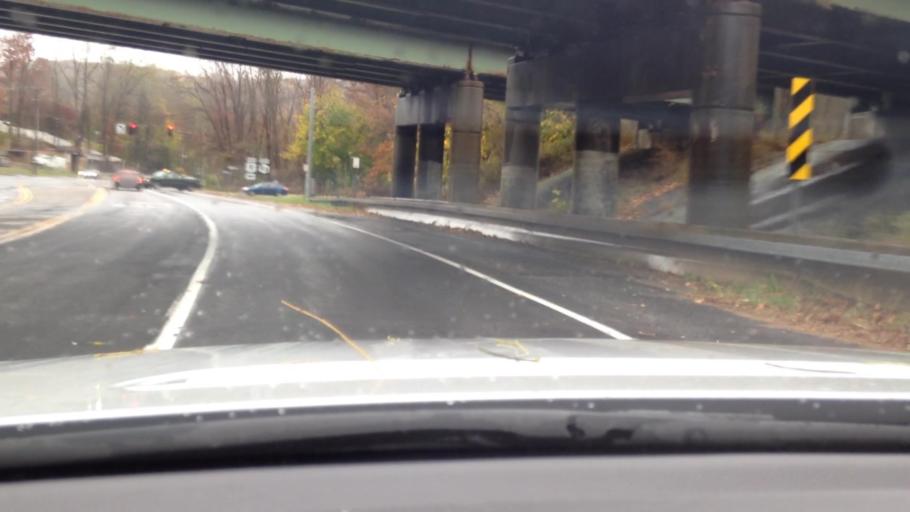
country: US
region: New York
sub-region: Westchester County
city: Crugers
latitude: 41.2312
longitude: -73.9119
